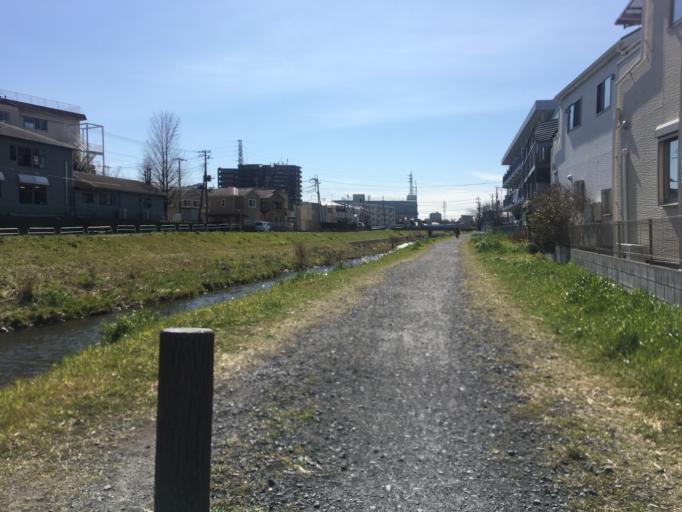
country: JP
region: Saitama
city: Asaka
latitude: 35.8018
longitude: 139.5816
